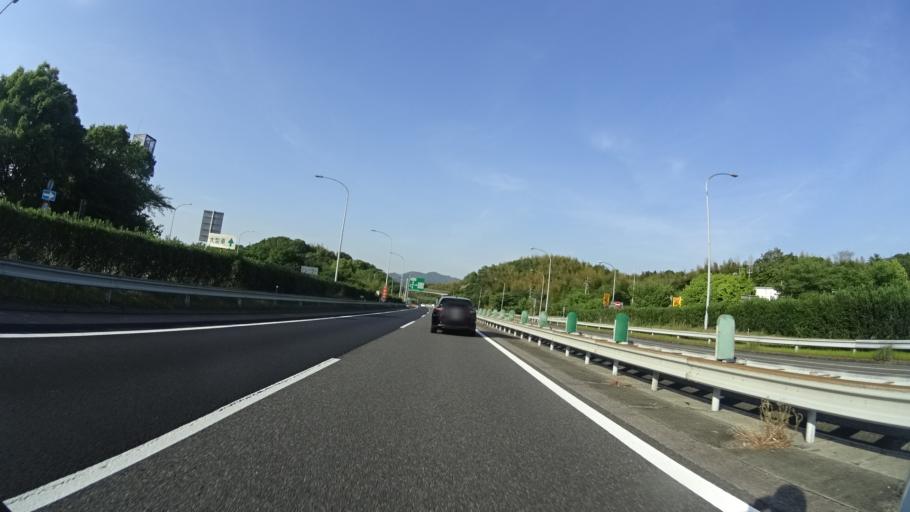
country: JP
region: Ehime
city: Kawanoecho
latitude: 33.9838
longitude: 133.5867
